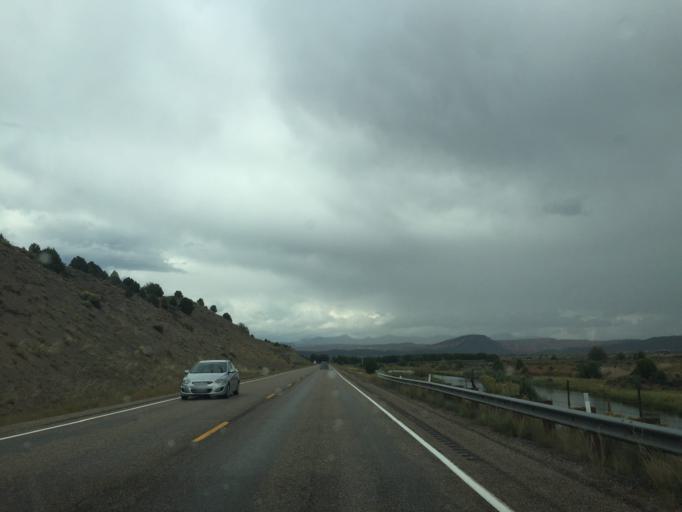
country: US
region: Utah
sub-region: Garfield County
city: Panguitch
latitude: 37.7045
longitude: -112.3951
